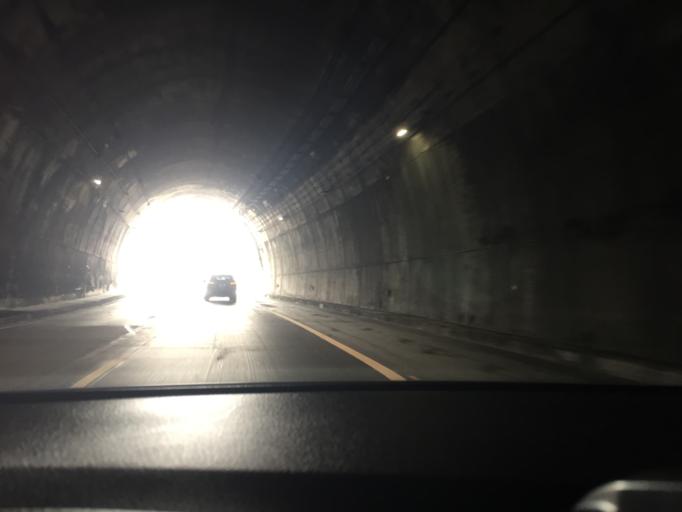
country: BR
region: Sao Paulo
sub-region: Santos
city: Santos
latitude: -23.8708
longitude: -46.3308
